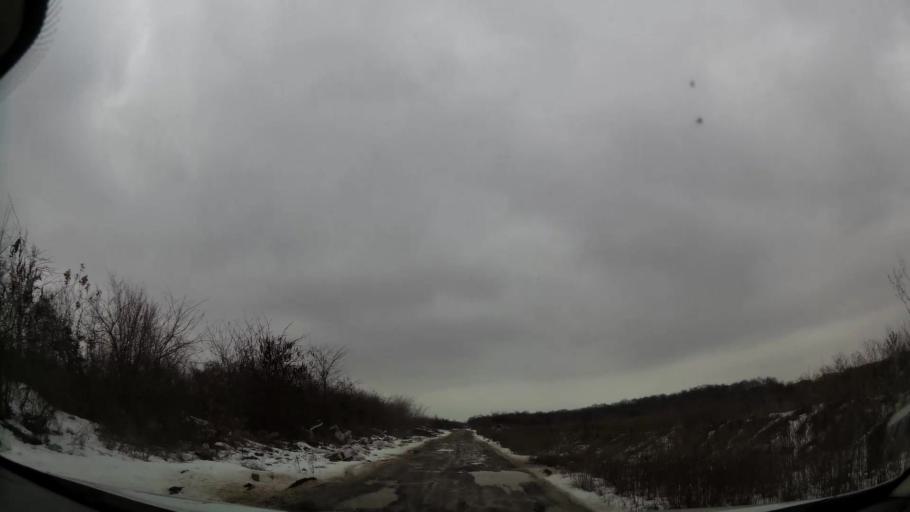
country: RO
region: Ilfov
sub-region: Comuna Chitila
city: Chitila
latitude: 44.5041
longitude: 26.0078
